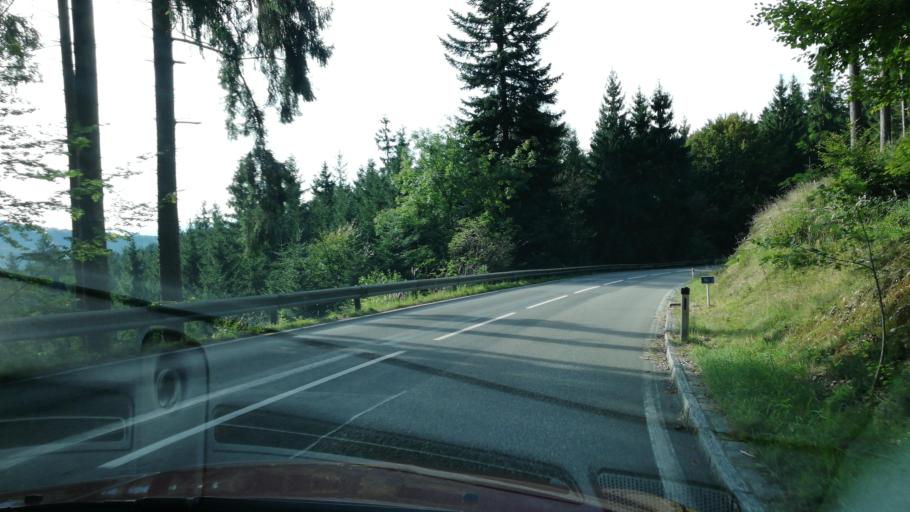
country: AT
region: Upper Austria
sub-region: Politischer Bezirk Vocklabruck
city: Redleiten
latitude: 48.1085
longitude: 13.5639
